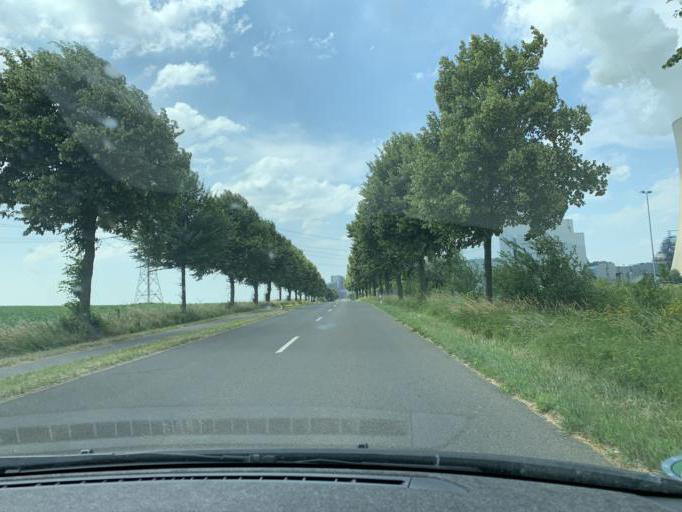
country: DE
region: North Rhine-Westphalia
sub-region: Regierungsbezirk Dusseldorf
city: Rommerskirchen
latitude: 51.0324
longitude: 6.6415
